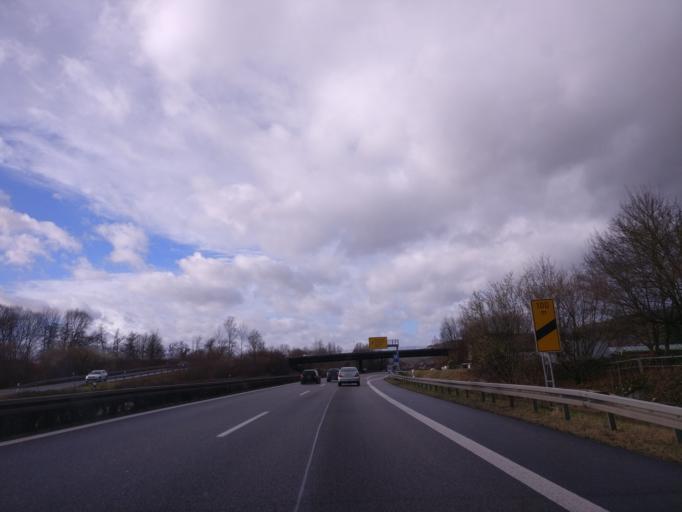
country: DE
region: Baden-Wuerttemberg
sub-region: Regierungsbezirk Stuttgart
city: Winterbach
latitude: 48.8085
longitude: 9.4365
